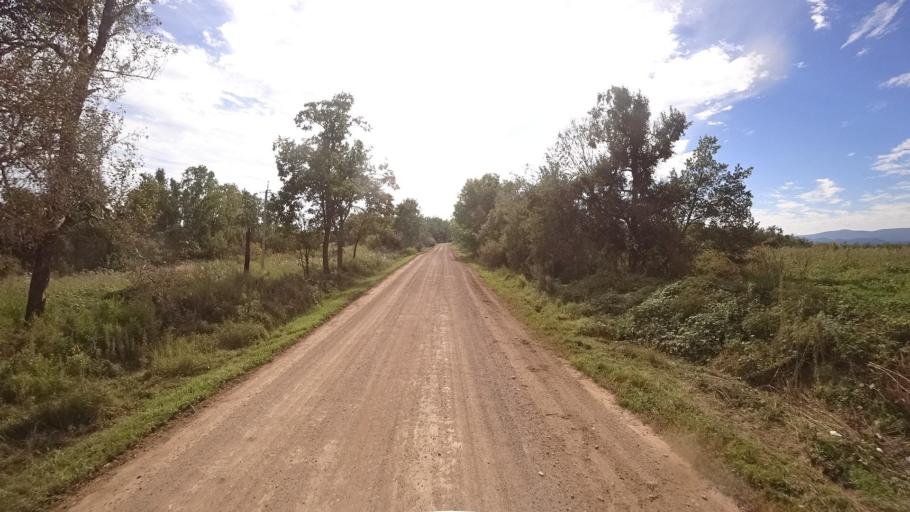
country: RU
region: Primorskiy
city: Dostoyevka
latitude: 44.3394
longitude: 133.5025
